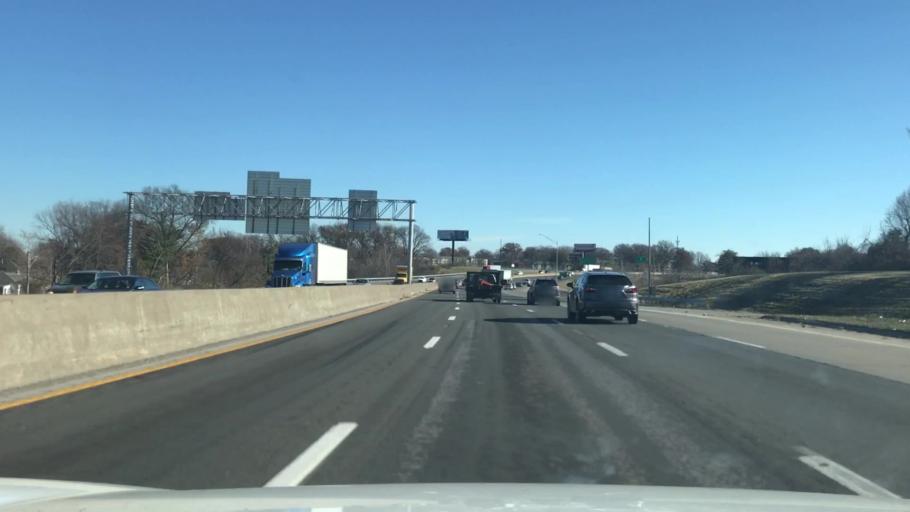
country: US
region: Missouri
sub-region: Saint Louis County
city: Normandy
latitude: 38.7161
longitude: -90.2959
